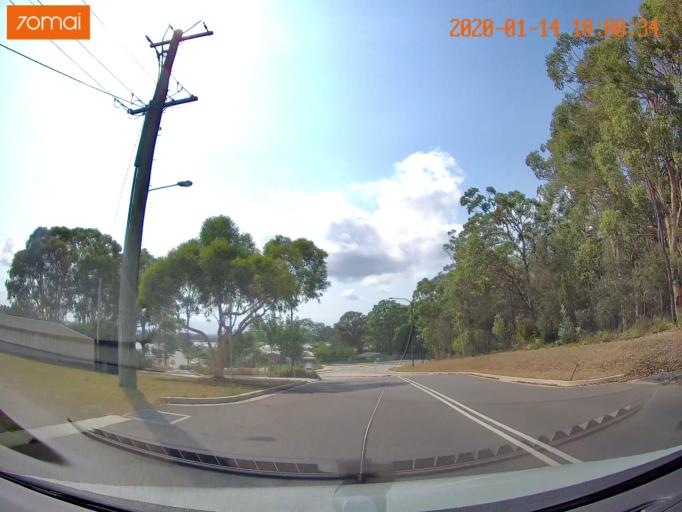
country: AU
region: New South Wales
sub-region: Wyong Shire
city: Kingfisher Shores
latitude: -33.1228
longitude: 151.5329
